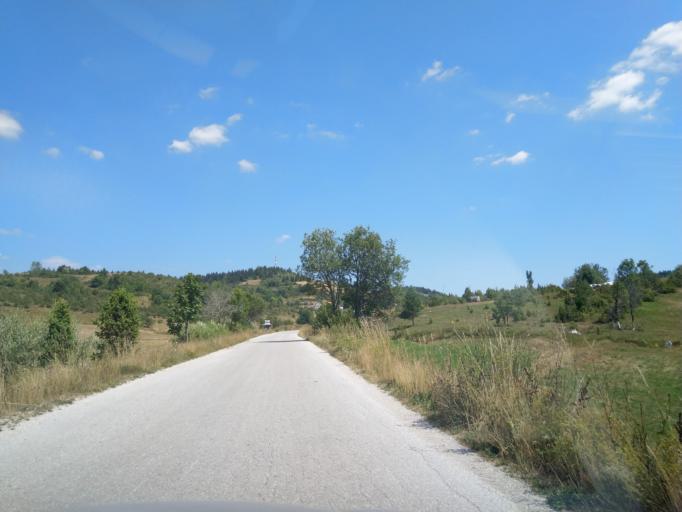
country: RS
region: Central Serbia
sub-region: Zlatiborski Okrug
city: Nova Varos
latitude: 43.4501
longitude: 19.9676
